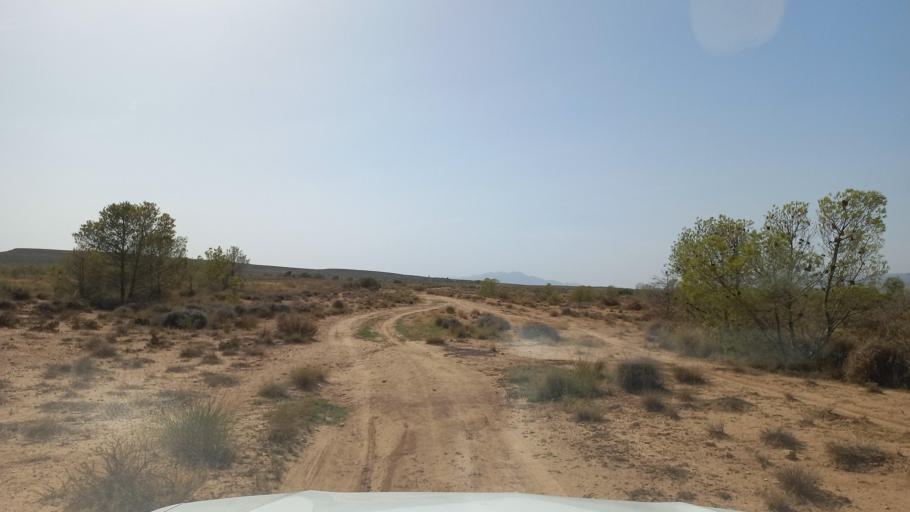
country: TN
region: Al Qasrayn
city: Kasserine
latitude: 35.2146
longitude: 9.0110
